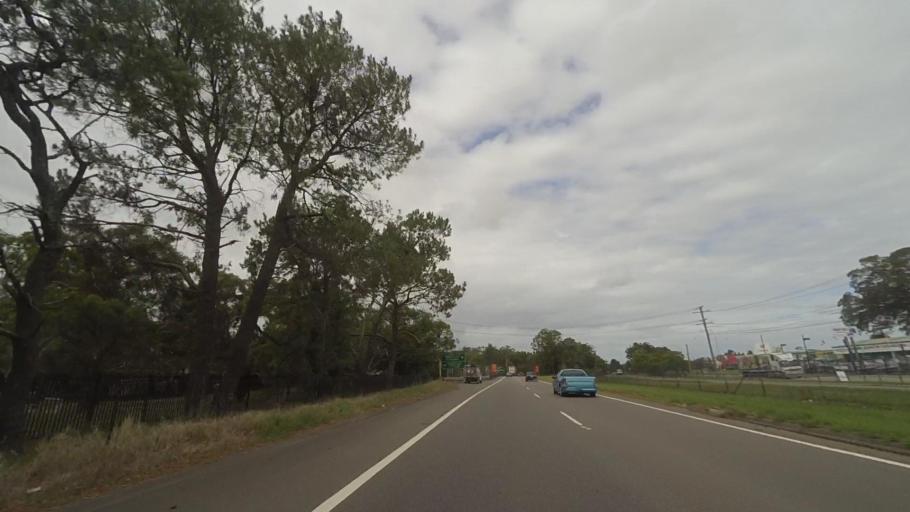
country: AU
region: New South Wales
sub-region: Port Stephens Shire
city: Raymond Terrace
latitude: -32.7831
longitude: 151.7352
